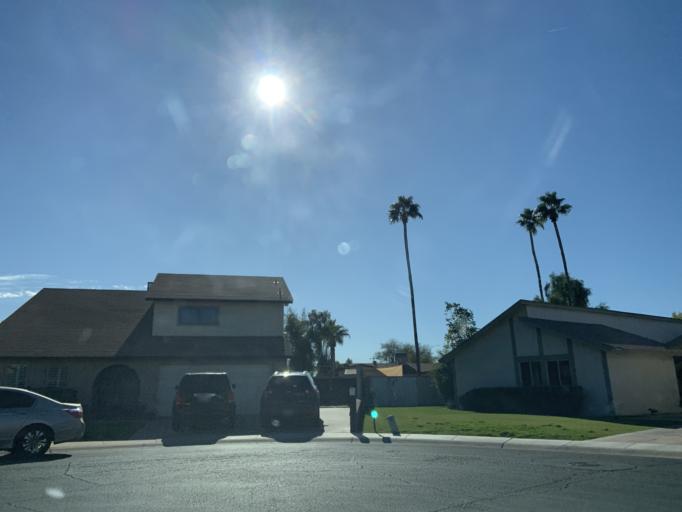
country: US
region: Arizona
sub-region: Maricopa County
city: San Carlos
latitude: 33.3669
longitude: -111.8649
